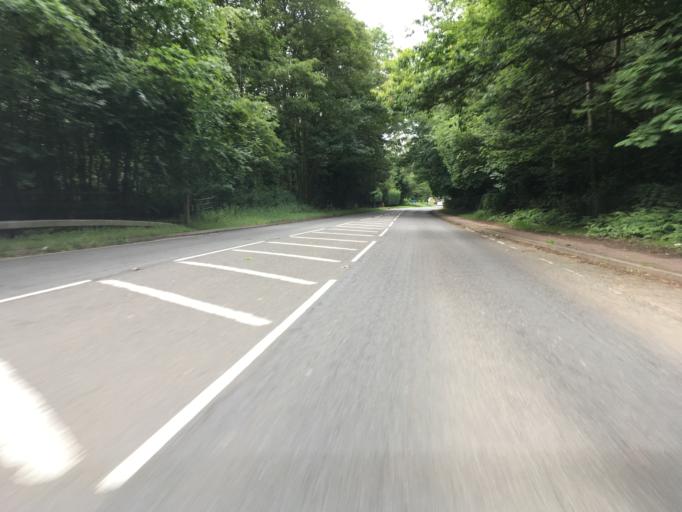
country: GB
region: England
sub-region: Milton Keynes
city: Woburn Sands
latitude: 52.0069
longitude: -0.6440
